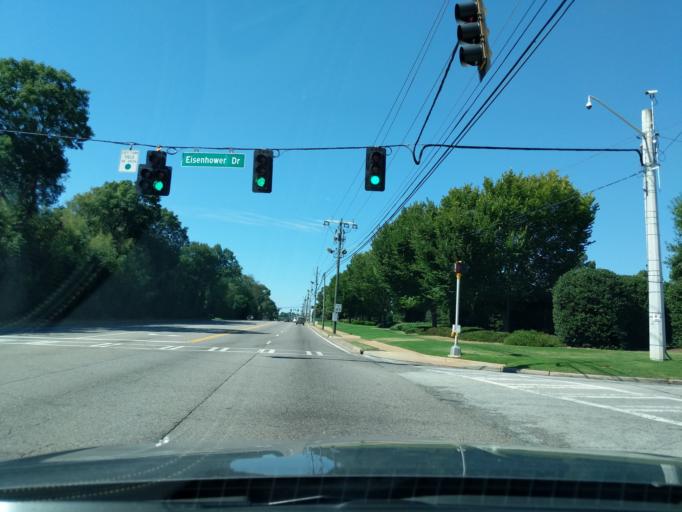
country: US
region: South Carolina
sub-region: Aiken County
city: North Augusta
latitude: 33.5049
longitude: -82.0167
